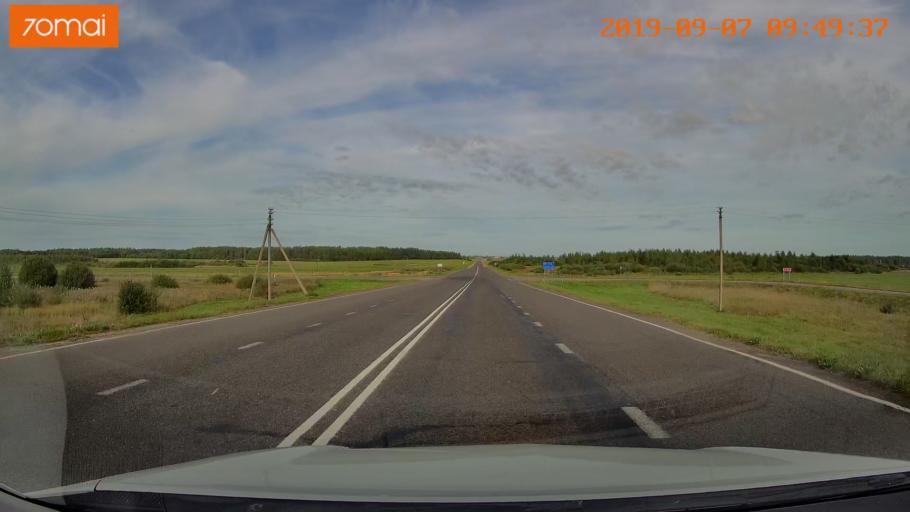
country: BY
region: Grodnenskaya
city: Iwye
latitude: 53.9844
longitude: 25.6599
